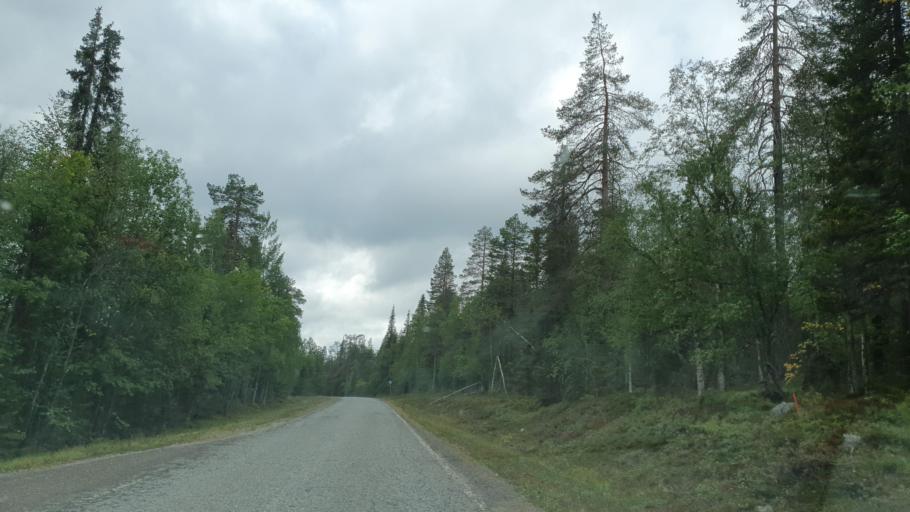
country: FI
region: Lapland
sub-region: Tunturi-Lappi
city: Muonio
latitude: 67.7270
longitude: 24.2418
